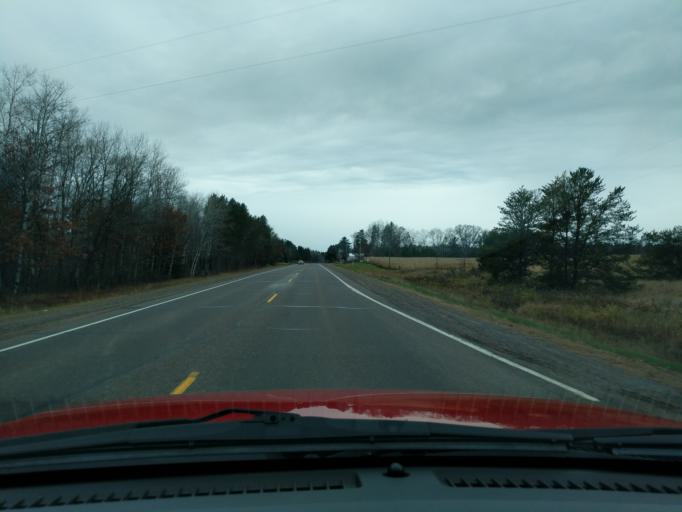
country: US
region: Wisconsin
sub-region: Washburn County
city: Spooner
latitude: 45.8218
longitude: -91.9185
